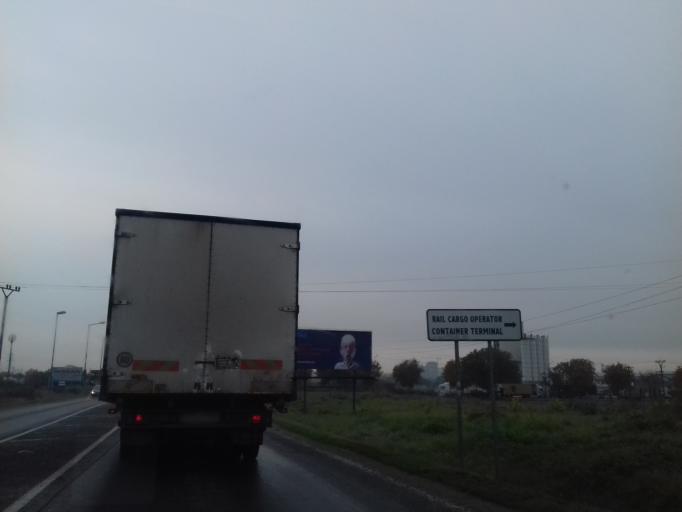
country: SK
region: Bratislavsky
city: Bratislava
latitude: 48.1349
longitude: 17.1626
